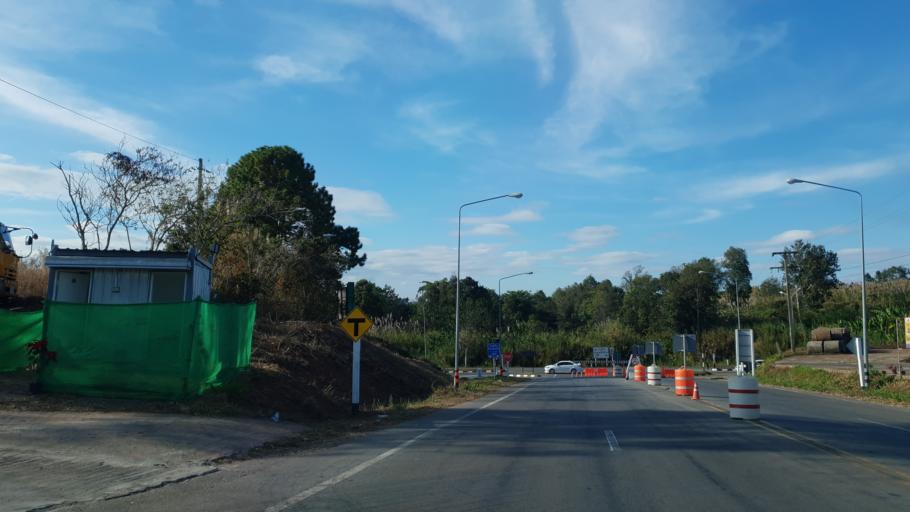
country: TH
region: Loei
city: Phu Ruea
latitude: 17.4470
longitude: 101.4913
